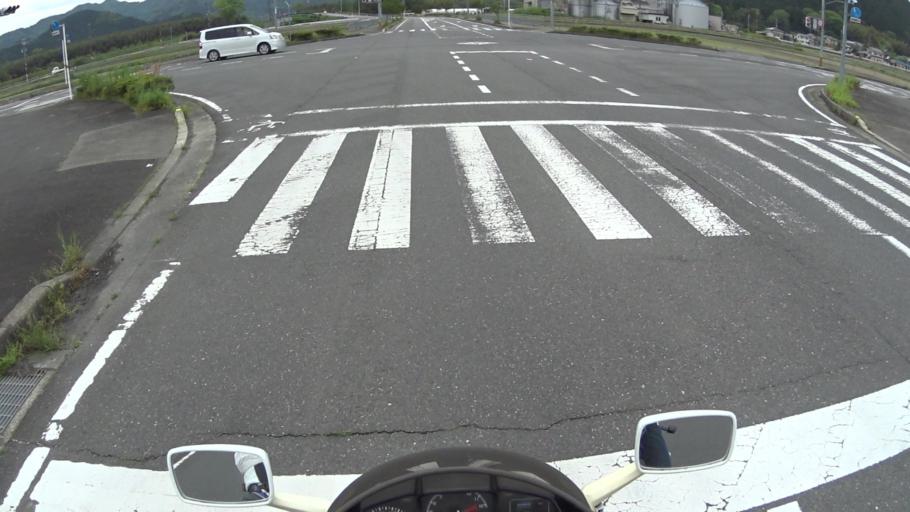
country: JP
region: Kyoto
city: Kameoka
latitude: 35.0773
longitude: 135.5368
